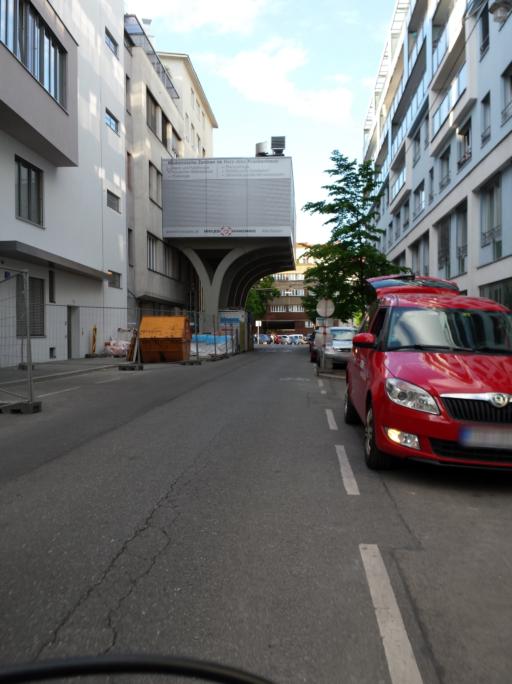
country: AT
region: Vienna
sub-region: Wien Stadt
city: Vienna
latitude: 48.1951
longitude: 16.3985
